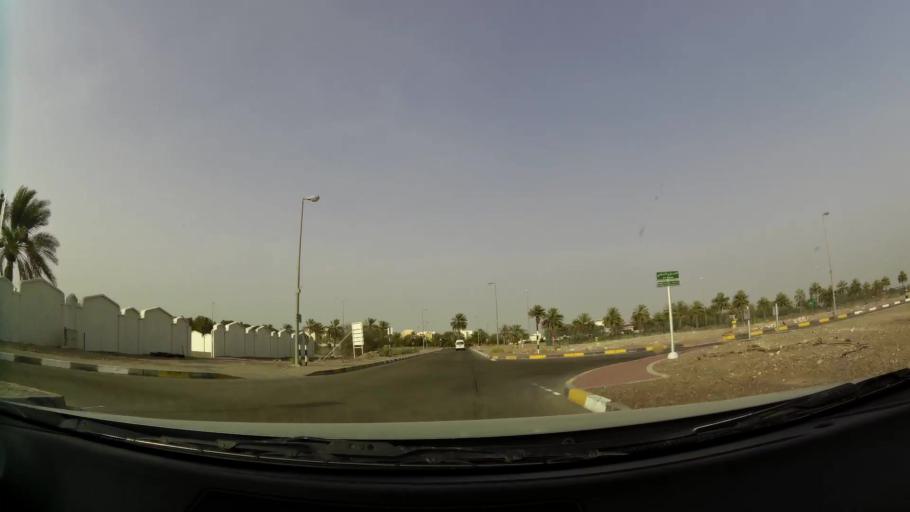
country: AE
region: Abu Dhabi
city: Al Ain
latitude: 24.2199
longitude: 55.6804
